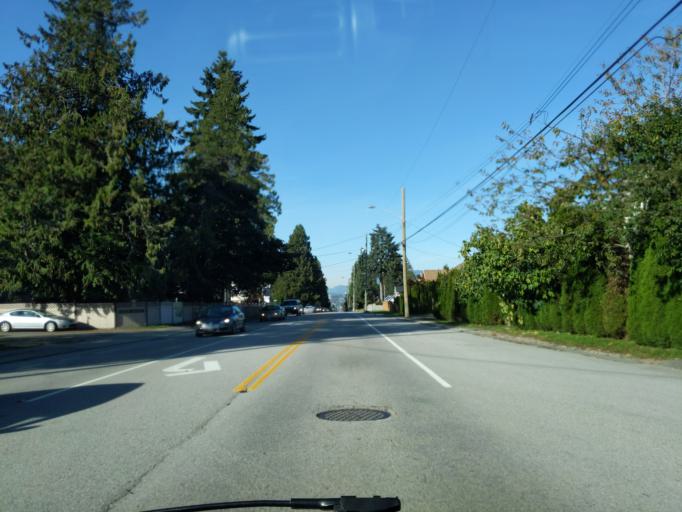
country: CA
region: British Columbia
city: New Westminster
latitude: 49.1936
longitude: -122.8677
